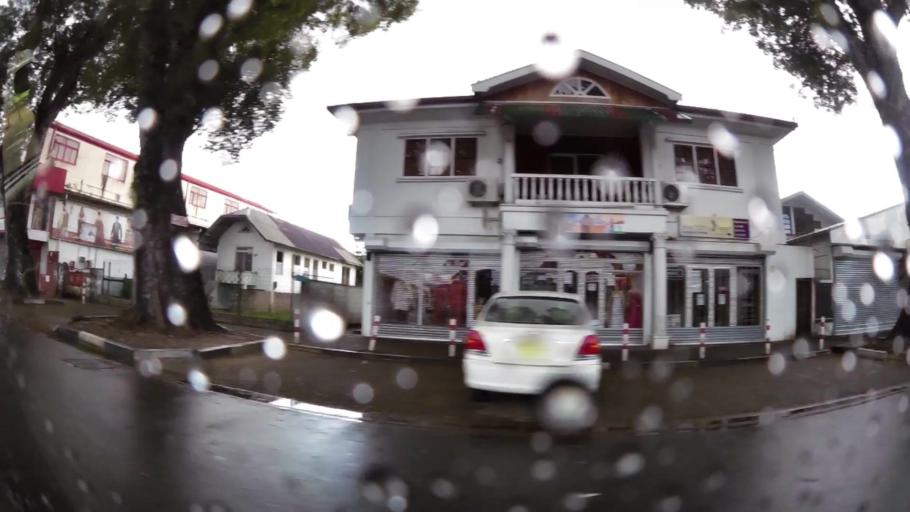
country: SR
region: Paramaribo
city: Paramaribo
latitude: 5.8294
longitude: -55.1588
